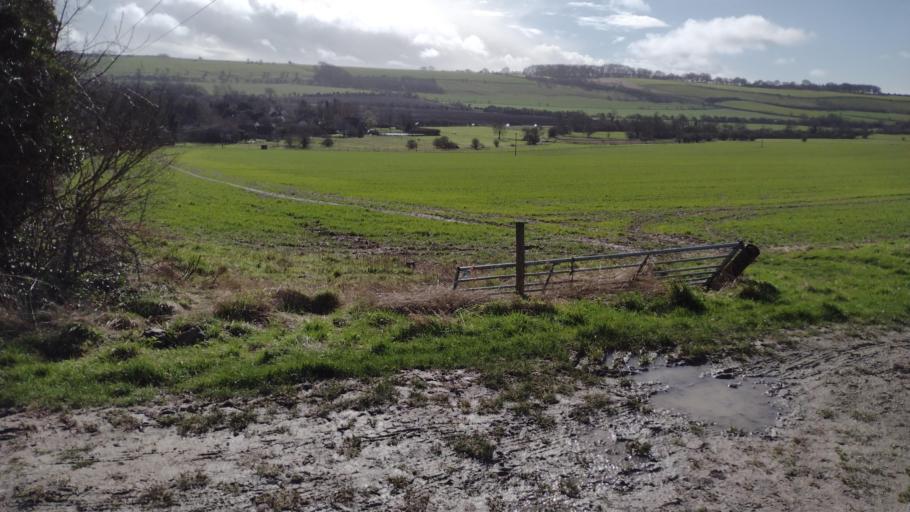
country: GB
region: England
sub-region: Wiltshire
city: Mildenhall
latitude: 51.4625
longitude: -1.7218
